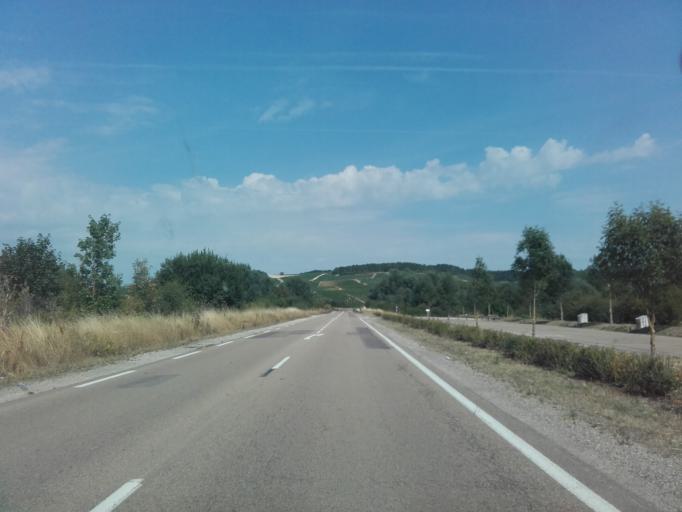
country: FR
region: Bourgogne
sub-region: Departement de l'Yonne
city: Chablis
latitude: 47.8220
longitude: 3.7833
